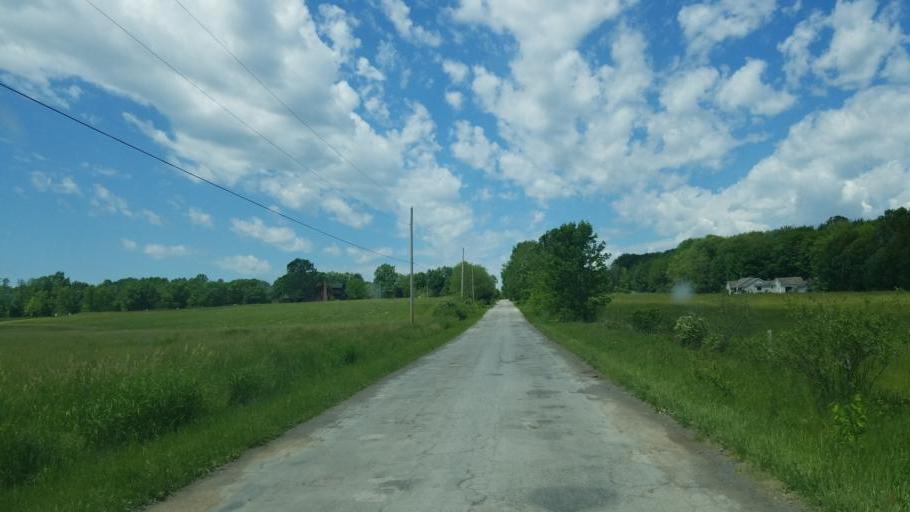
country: US
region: Ohio
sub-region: Geauga County
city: Middlefield
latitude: 41.4042
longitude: -80.9772
